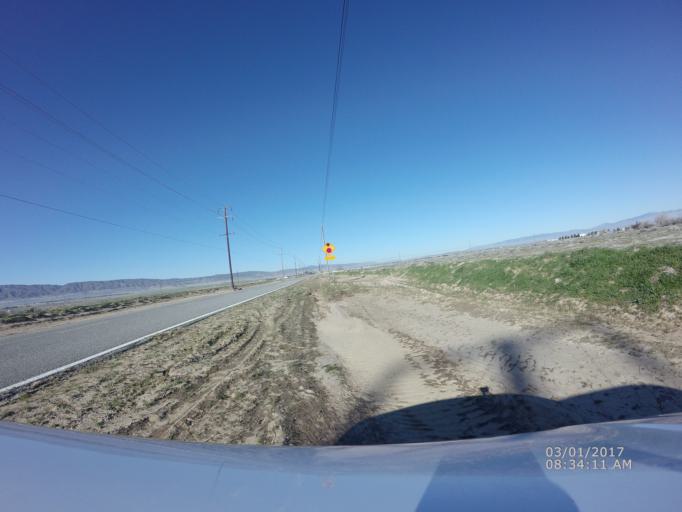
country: US
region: California
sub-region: Los Angeles County
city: Quartz Hill
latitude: 34.6894
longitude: -118.2518
